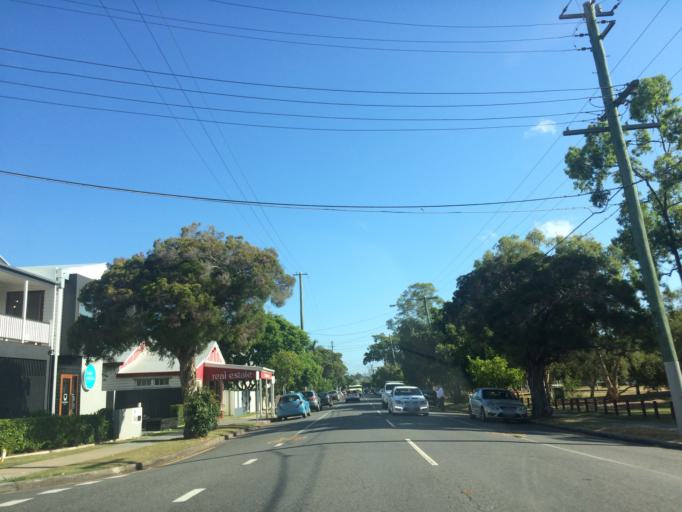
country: AU
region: Queensland
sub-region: Brisbane
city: Balmoral
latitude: -27.4646
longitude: 153.0599
